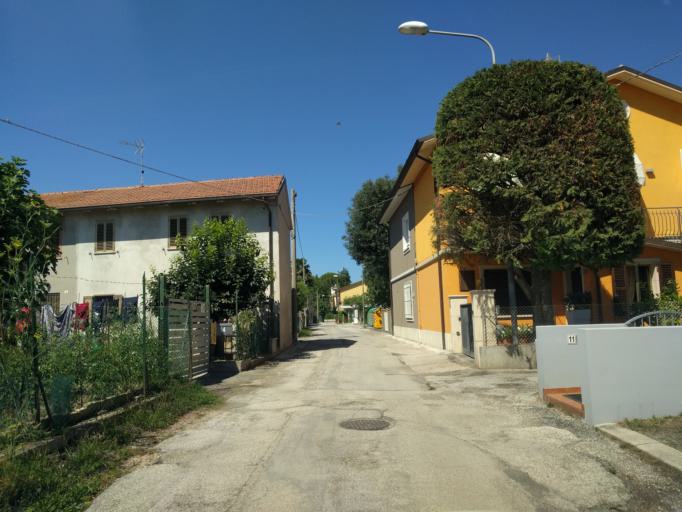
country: IT
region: The Marches
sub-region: Provincia di Pesaro e Urbino
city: Bellocchi
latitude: 43.7992
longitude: 12.9922
